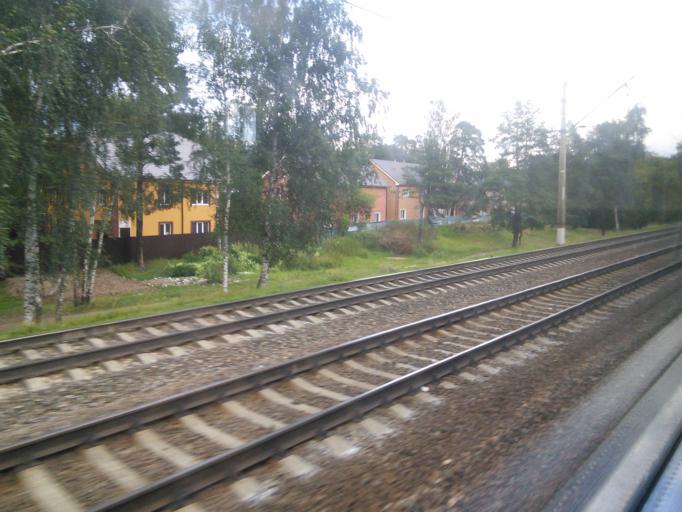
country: RU
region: Moskovskaya
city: Malakhovka
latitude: 55.6395
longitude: 38.0293
